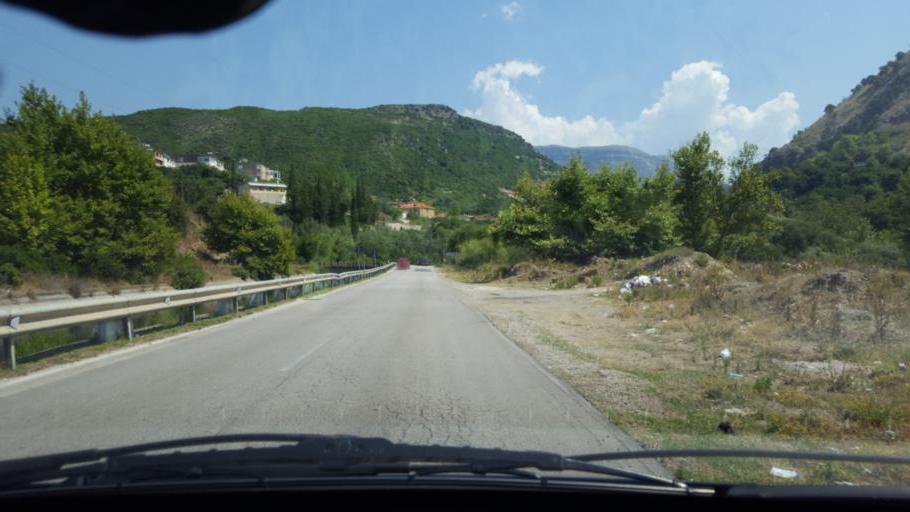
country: AL
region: Vlore
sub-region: Rrethi i Delvines
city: Mesopotam
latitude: 39.9148
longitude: 20.1319
